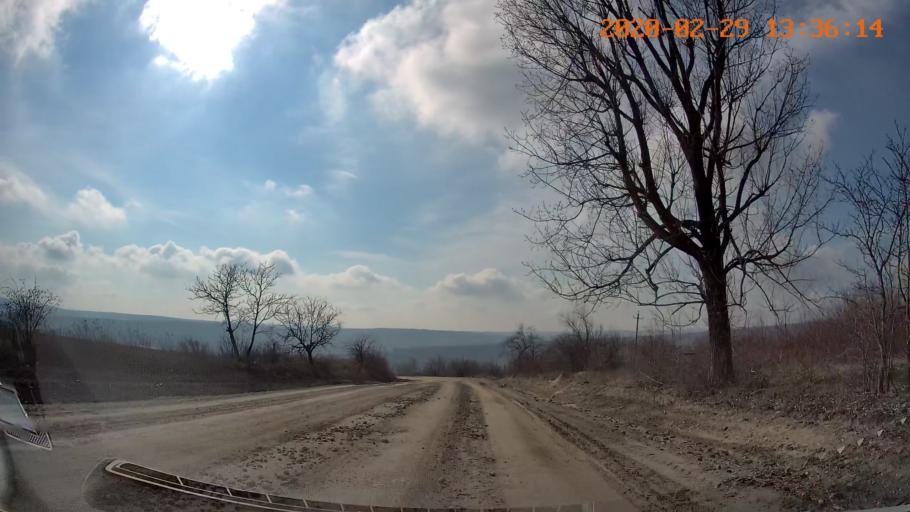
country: MD
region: Telenesti
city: Camenca
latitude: 47.8624
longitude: 28.6071
